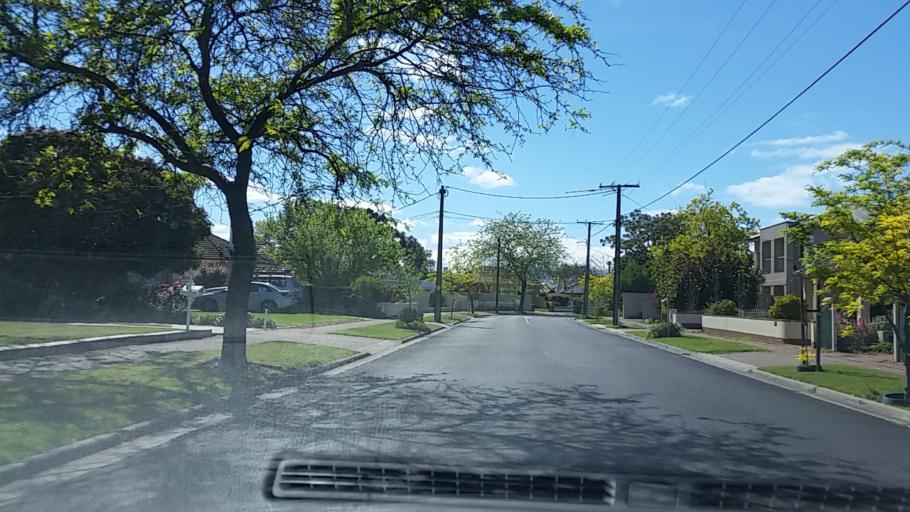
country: AU
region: South Australia
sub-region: Port Adelaide Enfield
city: Klemzig
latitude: -34.8848
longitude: 138.6158
